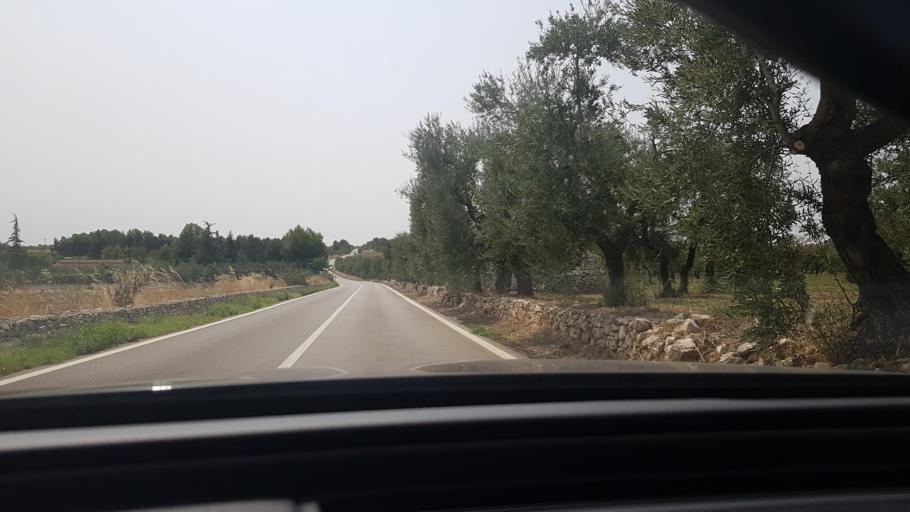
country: IT
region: Apulia
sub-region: Provincia di Barletta - Andria - Trani
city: Andria
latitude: 41.1113
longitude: 16.2808
